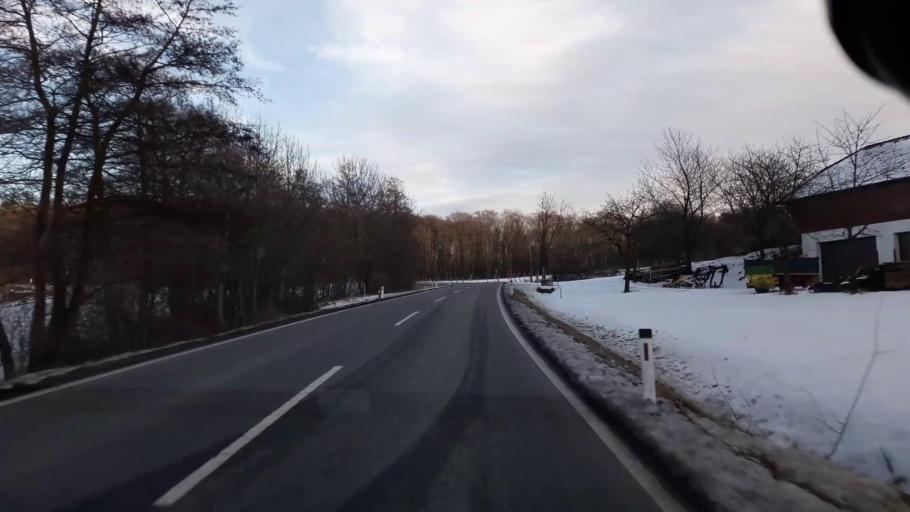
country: AT
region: Lower Austria
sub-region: Politischer Bezirk Wien-Umgebung
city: Mauerbach
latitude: 48.2800
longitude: 16.1749
